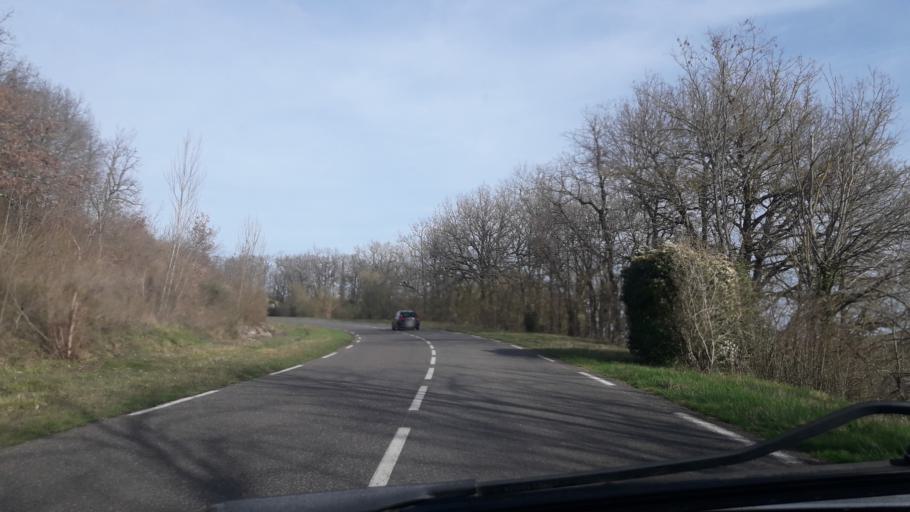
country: FR
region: Midi-Pyrenees
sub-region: Departement du Gers
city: Gimont
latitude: 43.7231
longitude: 0.9620
